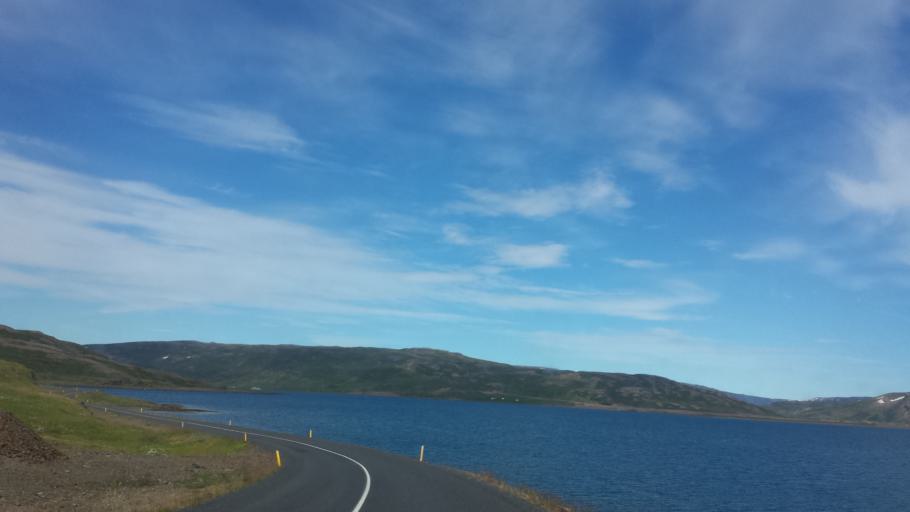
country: IS
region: West
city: Stykkisholmur
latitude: 65.7508
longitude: -21.7083
